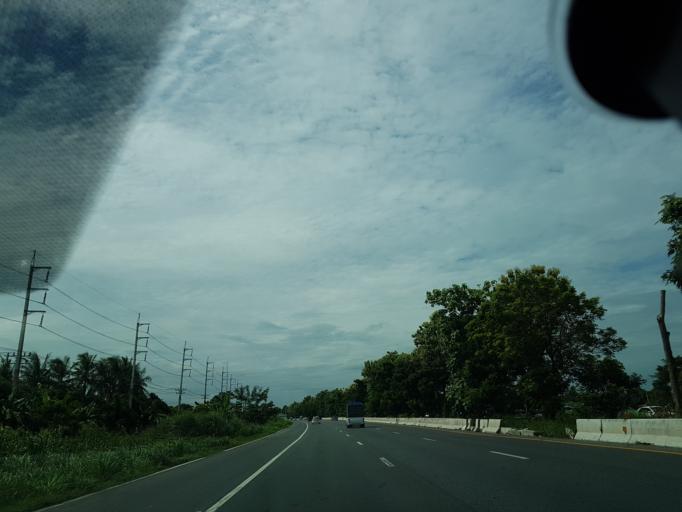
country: TH
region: Ang Thong
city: Chaiyo
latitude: 14.6996
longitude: 100.4566
